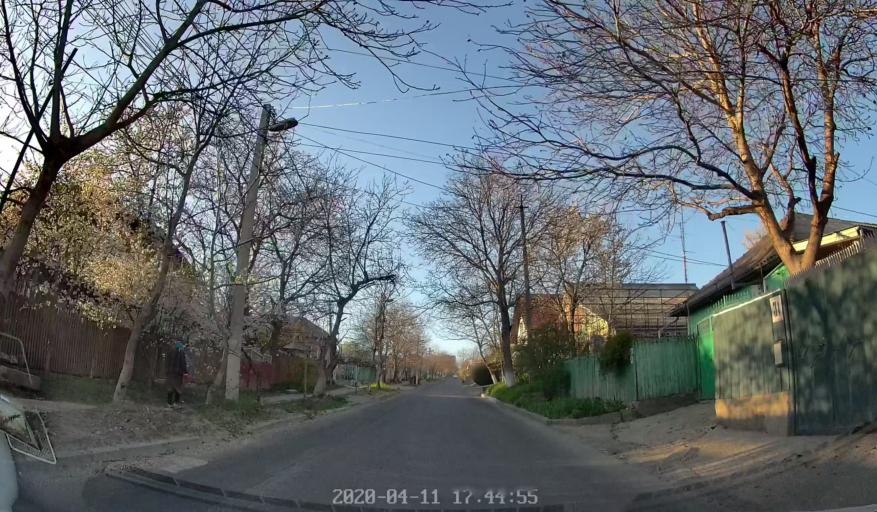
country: MD
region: Chisinau
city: Chisinau
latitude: 46.9809
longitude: 28.8233
